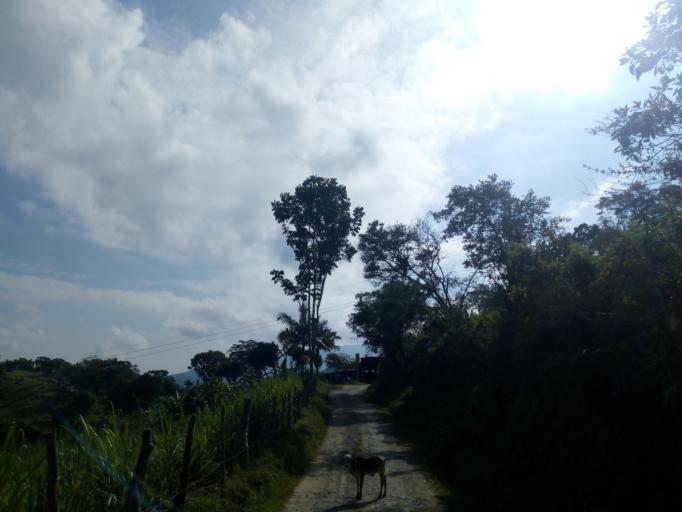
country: CO
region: Boyaca
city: Moniquira
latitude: 5.8856
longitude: -73.5134
